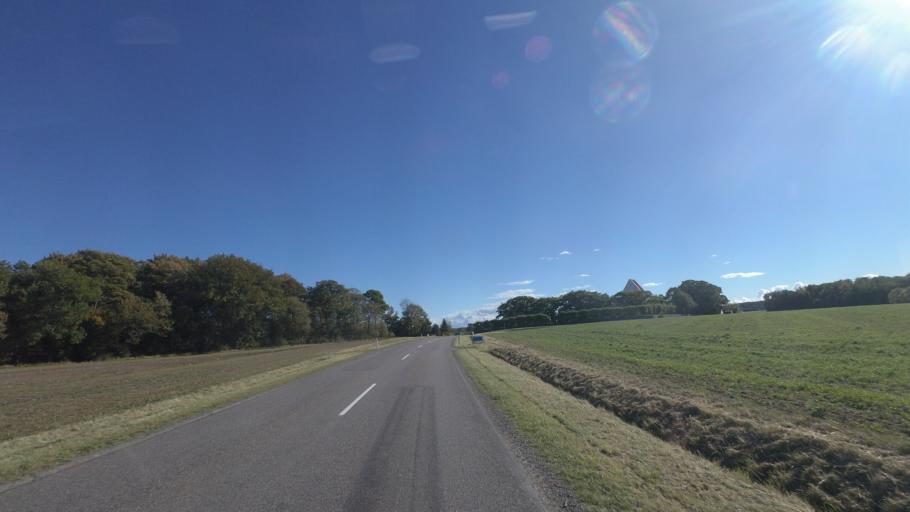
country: DK
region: Capital Region
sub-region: Bornholm Kommune
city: Nexo
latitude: 55.1191
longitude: 15.1043
